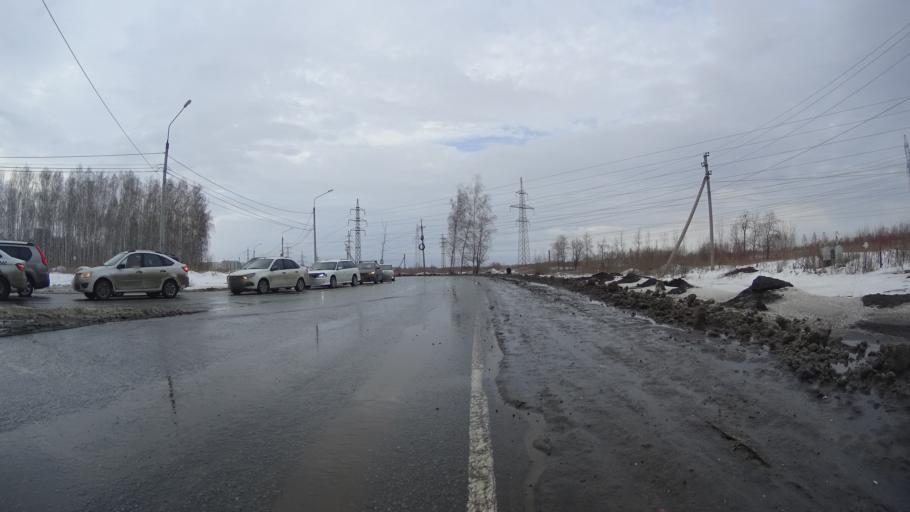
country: RU
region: Chelyabinsk
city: Roshchino
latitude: 55.2087
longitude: 61.3174
